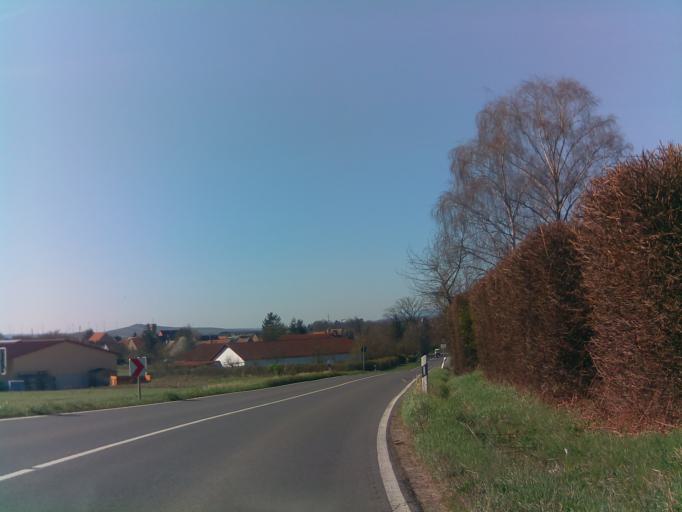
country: DE
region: Rheinland-Pfalz
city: Kongernheim
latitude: 49.8509
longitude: 8.2509
